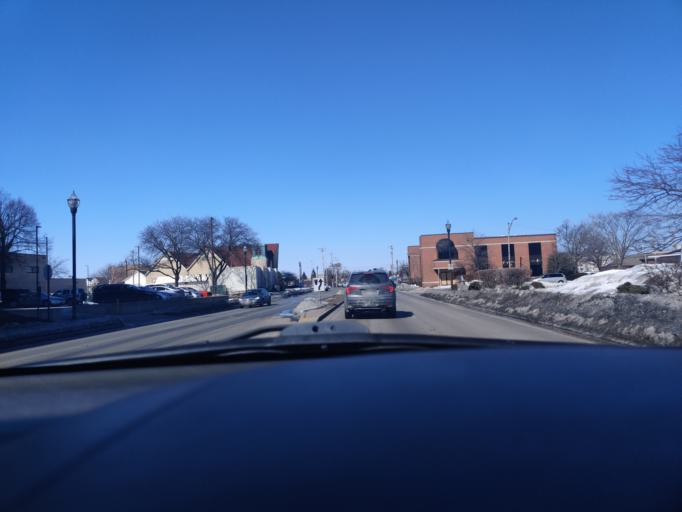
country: US
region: Wisconsin
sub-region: Kenosha County
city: Kenosha
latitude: 42.5850
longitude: -87.8223
